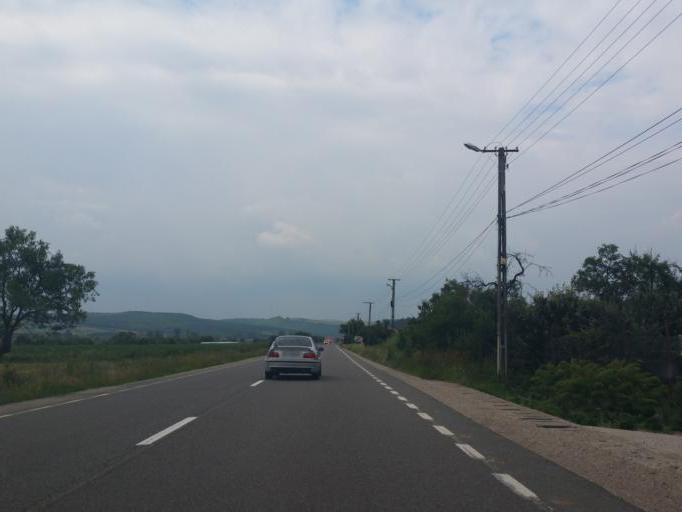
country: RO
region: Salaj
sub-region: Comuna Romanasi
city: Romanasi
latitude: 47.0949
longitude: 23.1888
